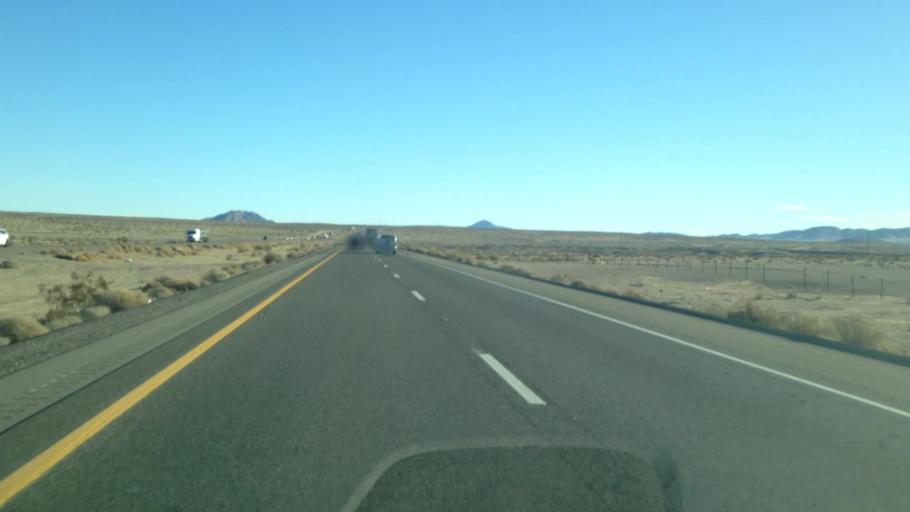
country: US
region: California
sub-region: San Bernardino County
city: Fort Irwin
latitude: 34.9941
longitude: -116.5746
